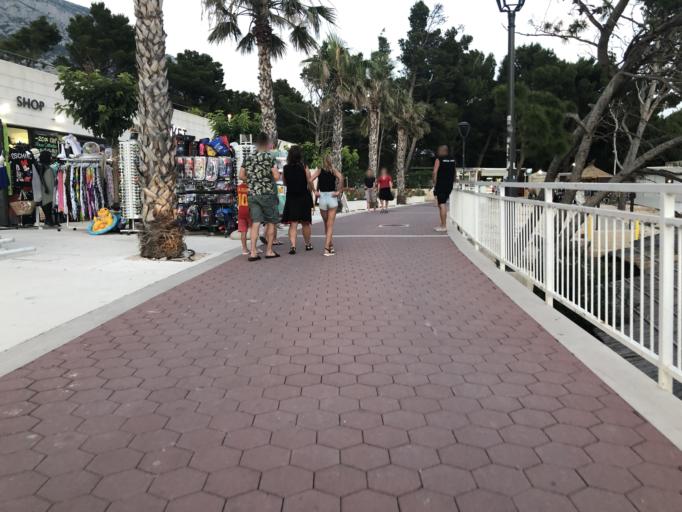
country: HR
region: Splitsko-Dalmatinska
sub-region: Grad Makarska
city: Makarska
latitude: 43.3062
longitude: 17.0022
